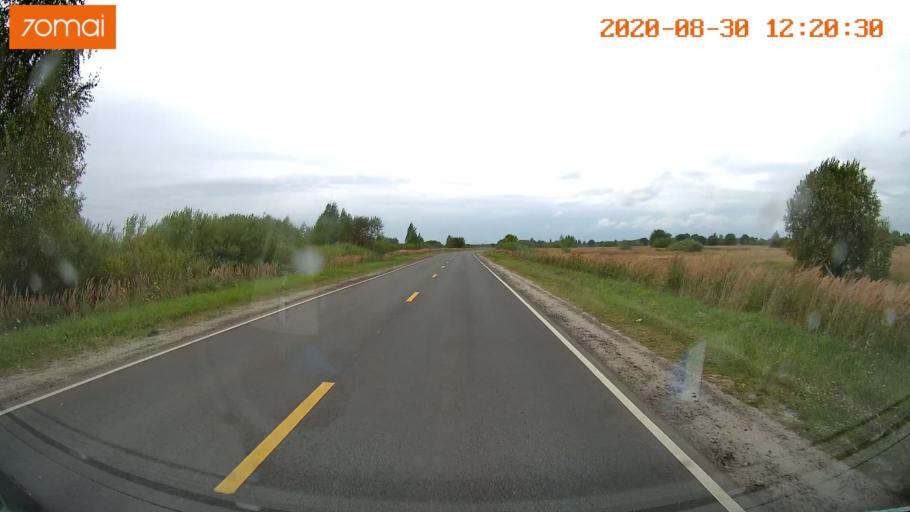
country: RU
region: Ivanovo
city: Yur'yevets
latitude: 57.3228
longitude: 42.8992
